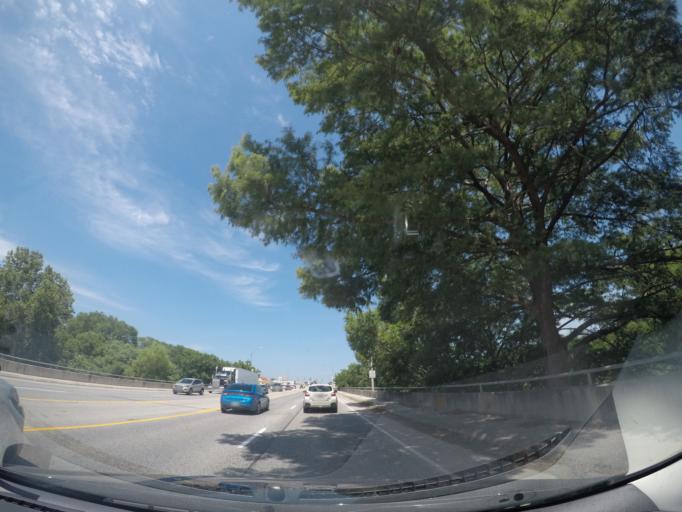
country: US
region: Texas
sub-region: Medina County
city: Castroville
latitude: 29.3554
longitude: -98.8737
